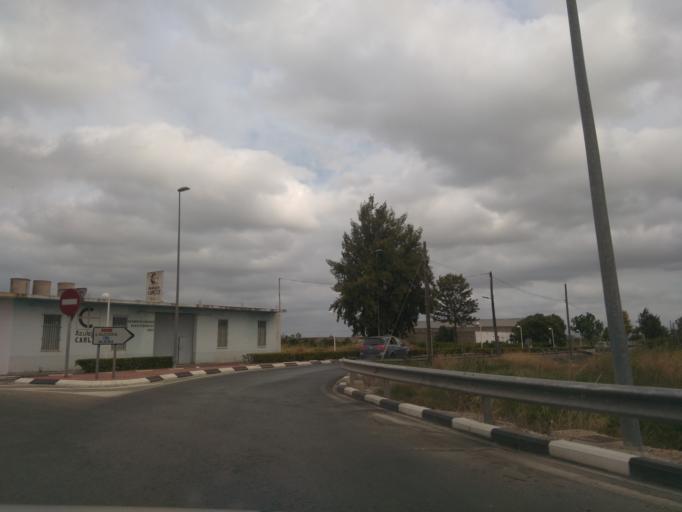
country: ES
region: Valencia
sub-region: Provincia de Valencia
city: Carlet
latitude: 39.2180
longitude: -0.5168
